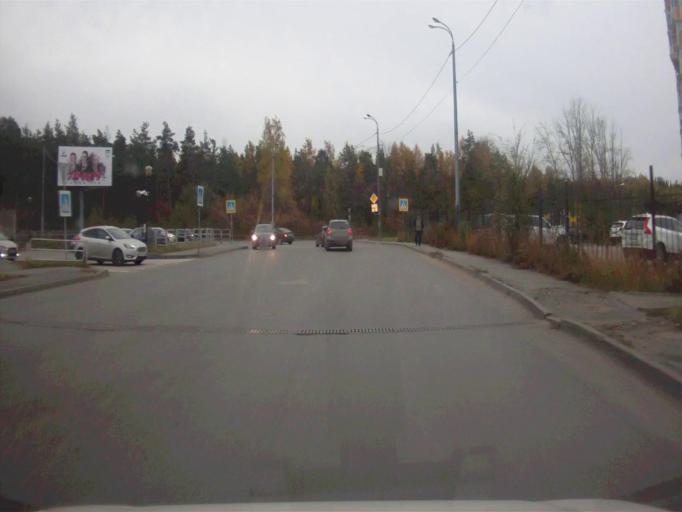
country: RU
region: Chelyabinsk
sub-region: Gorod Chelyabinsk
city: Chelyabinsk
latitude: 55.1696
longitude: 61.3542
